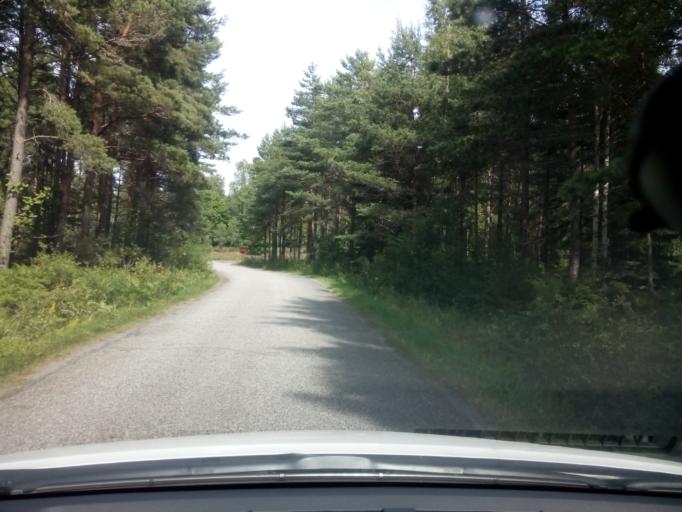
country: SE
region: Soedermanland
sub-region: Trosa Kommun
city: Trosa
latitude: 58.7648
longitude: 17.3701
